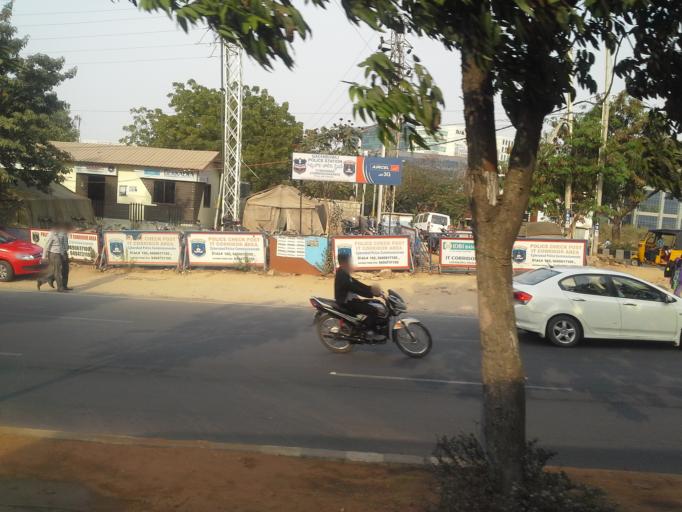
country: IN
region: Telangana
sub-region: Medak
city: Serilingampalle
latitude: 17.4455
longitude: 78.3520
